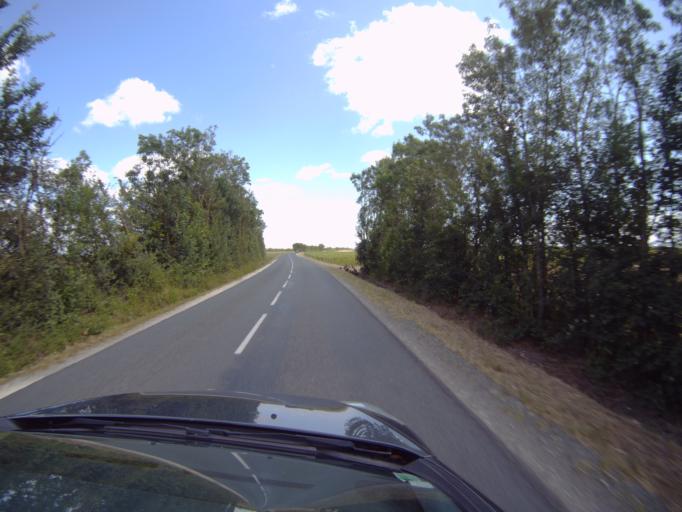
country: FR
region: Poitou-Charentes
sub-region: Departement de la Charente-Maritime
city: Saint-Jean-de-Liversay
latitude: 46.2608
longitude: -0.8623
